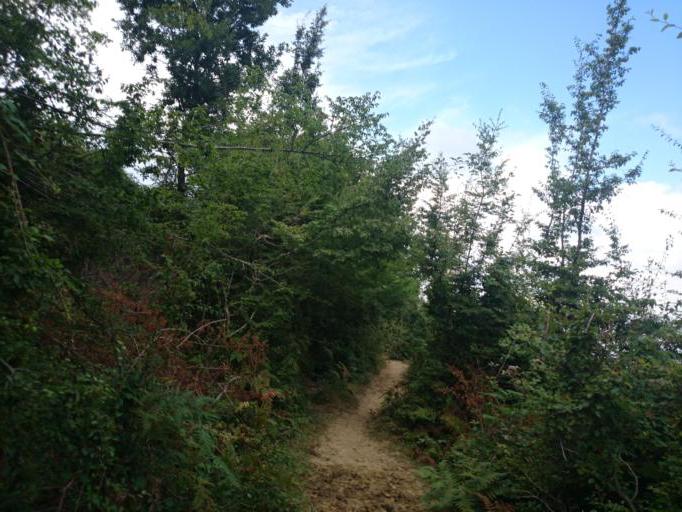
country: AL
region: Elbasan
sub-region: Rrethi i Elbasanit
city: Gjinar
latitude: 40.9895
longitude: 20.2029
